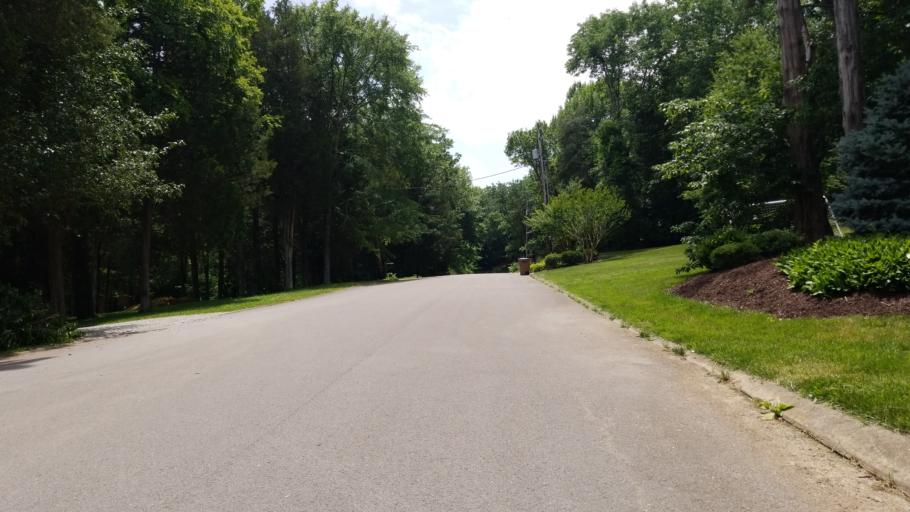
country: US
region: Tennessee
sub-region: Davidson County
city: Forest Hills
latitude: 36.0388
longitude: -86.8628
